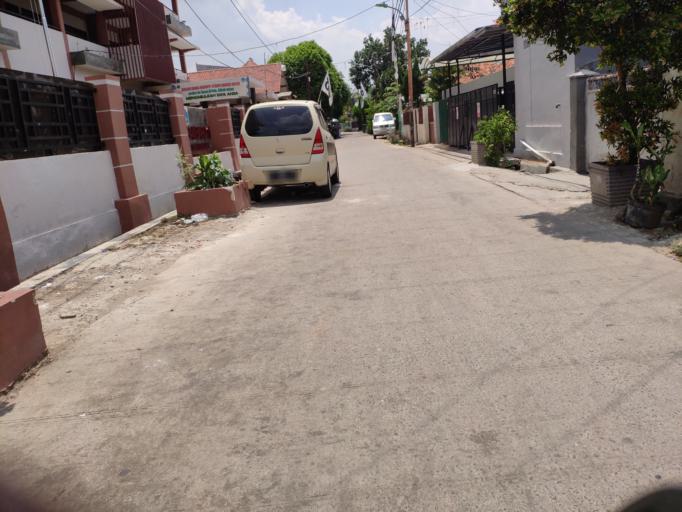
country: ID
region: Jakarta Raya
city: Jakarta
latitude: -6.2130
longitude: 106.8710
